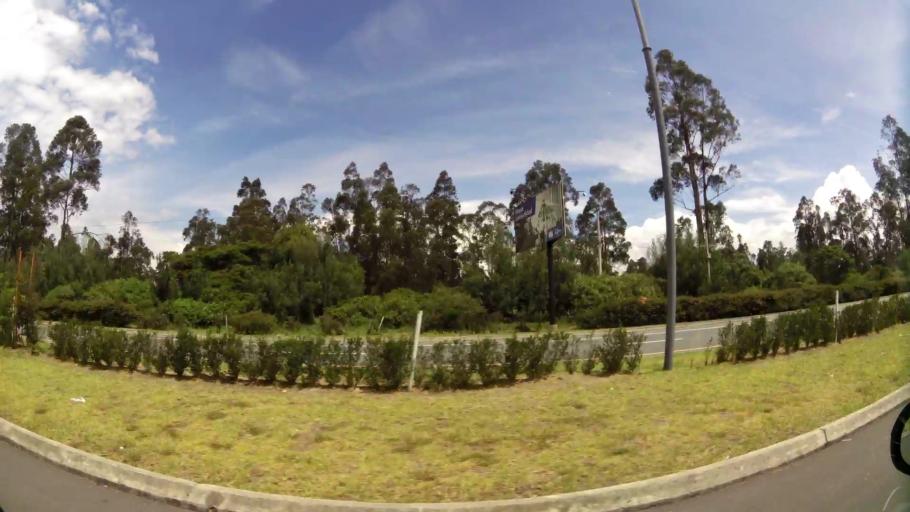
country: EC
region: Pichincha
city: Quito
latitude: -0.1619
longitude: -78.3465
